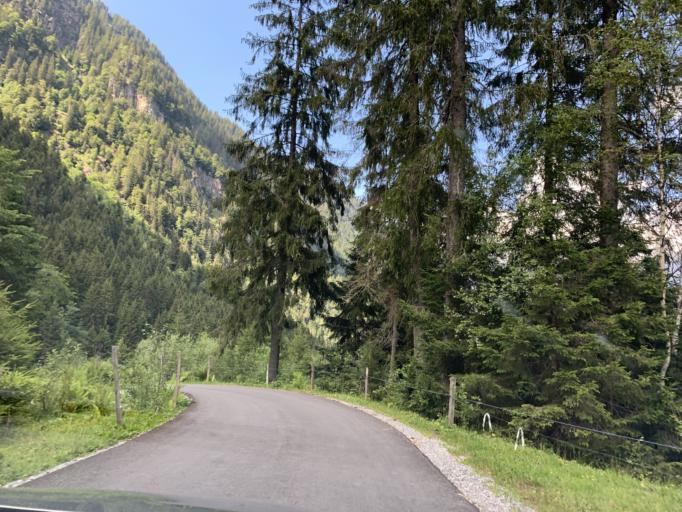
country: CH
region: Saint Gallen
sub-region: Wahlkreis Sarganserland
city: Quarten
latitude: 47.0792
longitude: 9.1994
